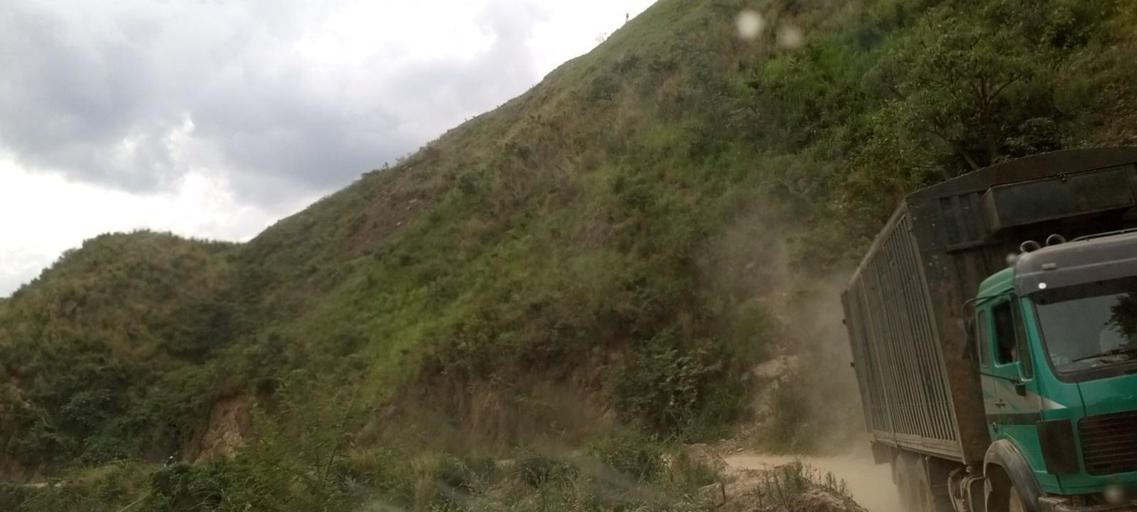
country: RW
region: Western Province
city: Cyangugu
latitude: -2.7055
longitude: 28.9456
